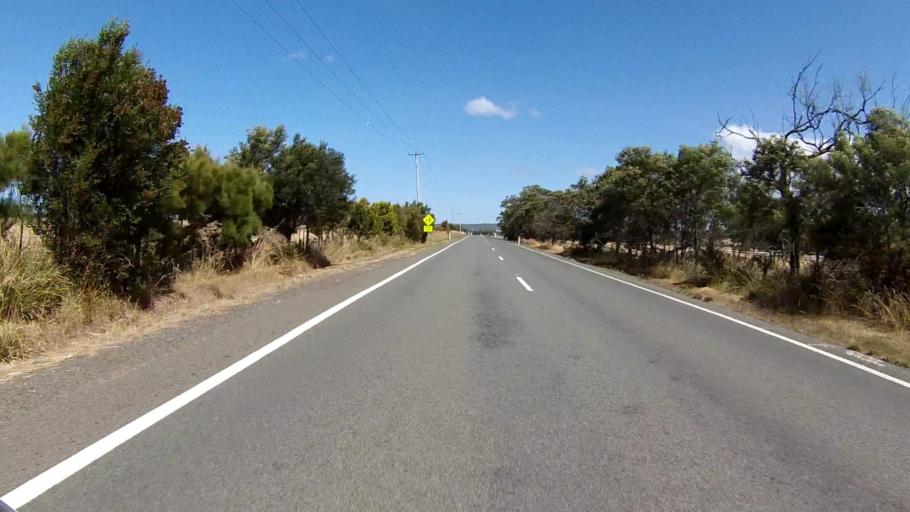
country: AU
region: Tasmania
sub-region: Break O'Day
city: St Helens
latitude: -42.0960
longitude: 148.0640
